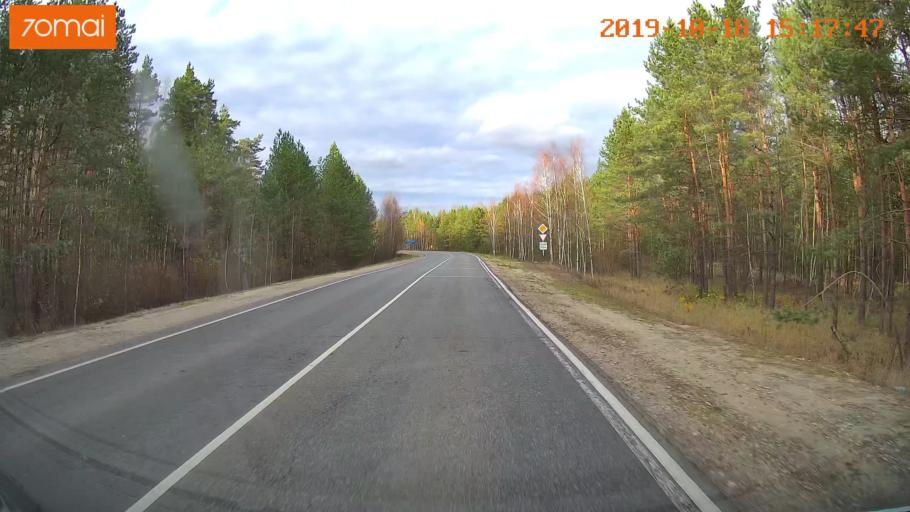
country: RU
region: Vladimir
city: Anopino
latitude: 55.6550
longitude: 40.7273
